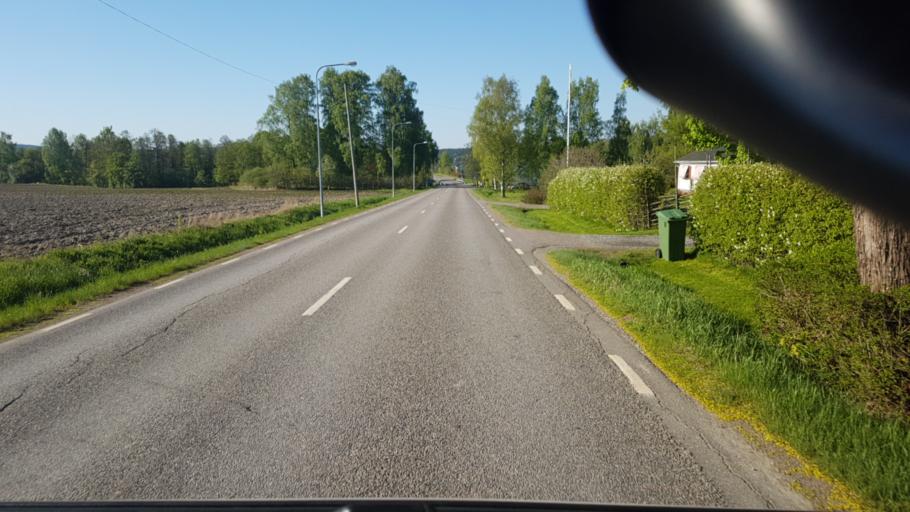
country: SE
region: Vaermland
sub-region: Arvika Kommun
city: Arvika
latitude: 59.7616
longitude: 12.5456
